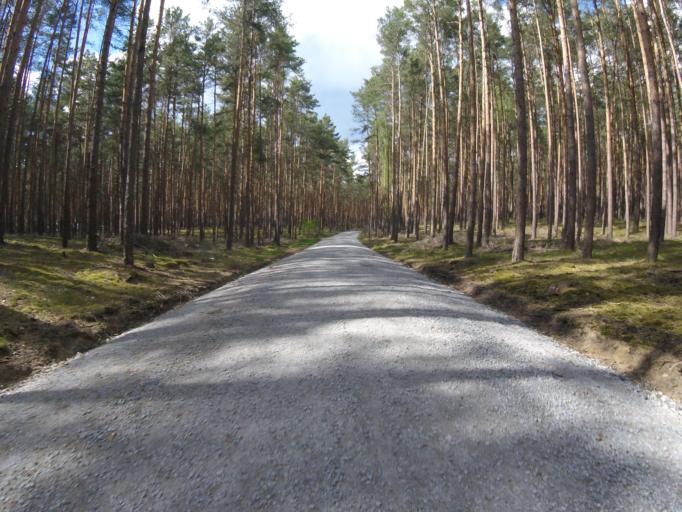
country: DE
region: Brandenburg
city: Schwerin
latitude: 52.1897
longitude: 13.5969
